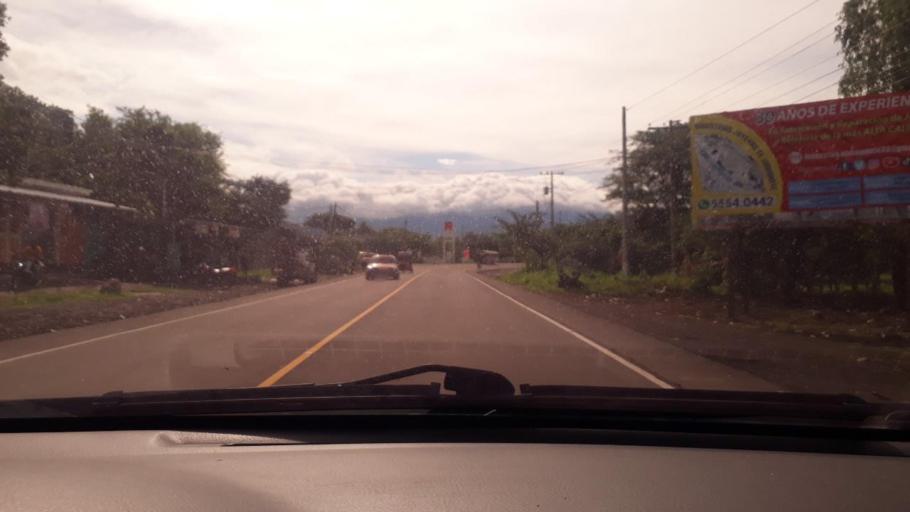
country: SV
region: Ahuachapan
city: San Francisco Menendez
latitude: 13.8808
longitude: -90.1008
